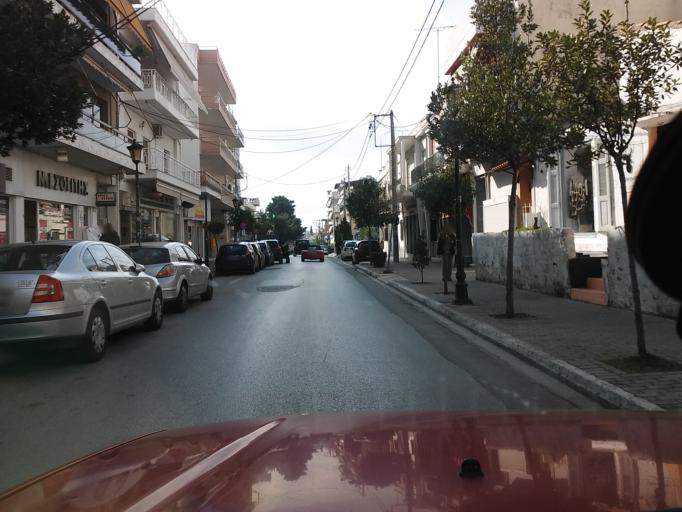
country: GR
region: Attica
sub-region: Nomarchia Athinas
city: Metamorfosi
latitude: 38.0618
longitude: 23.7594
